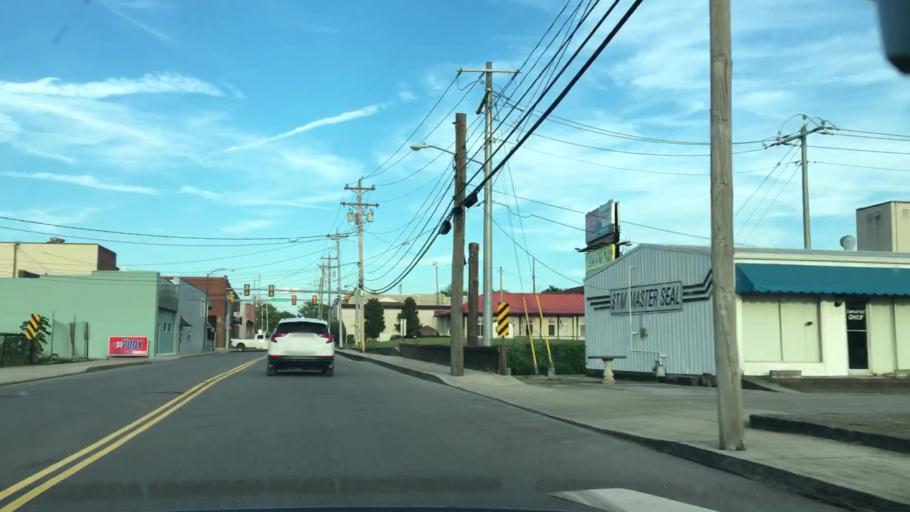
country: US
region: Tennessee
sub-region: Wilson County
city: Lebanon
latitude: 36.2069
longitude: -86.2925
